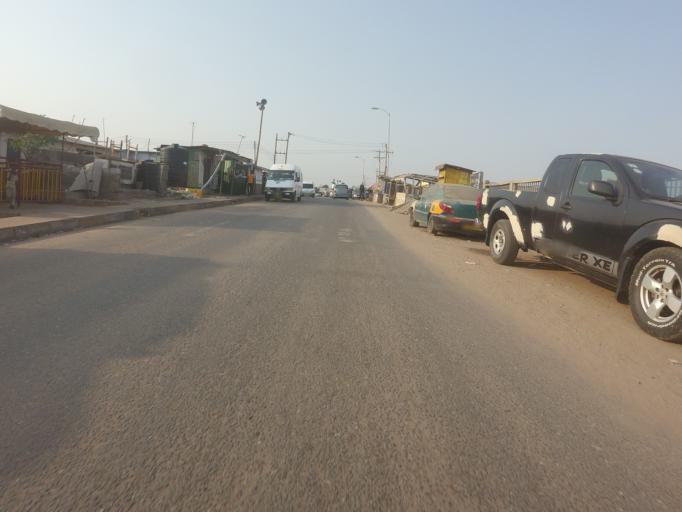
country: GH
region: Greater Accra
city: Nungua
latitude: 5.6134
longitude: -0.0469
